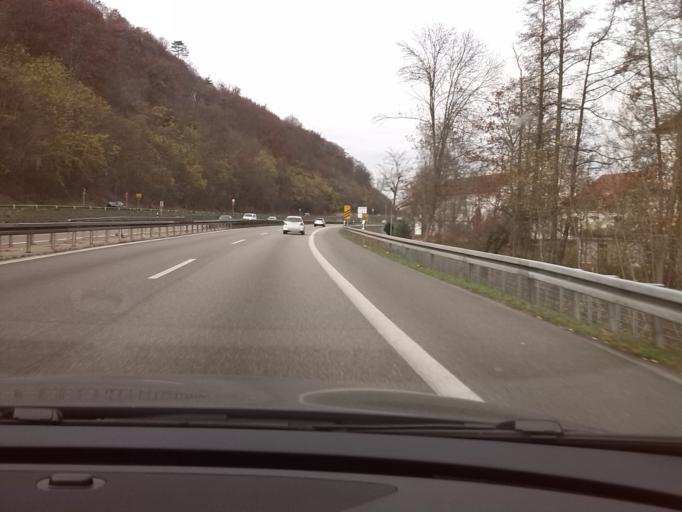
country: DE
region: Baden-Wuerttemberg
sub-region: Regierungsbezirk Stuttgart
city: Ostfildern
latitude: 48.7438
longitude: 9.2677
